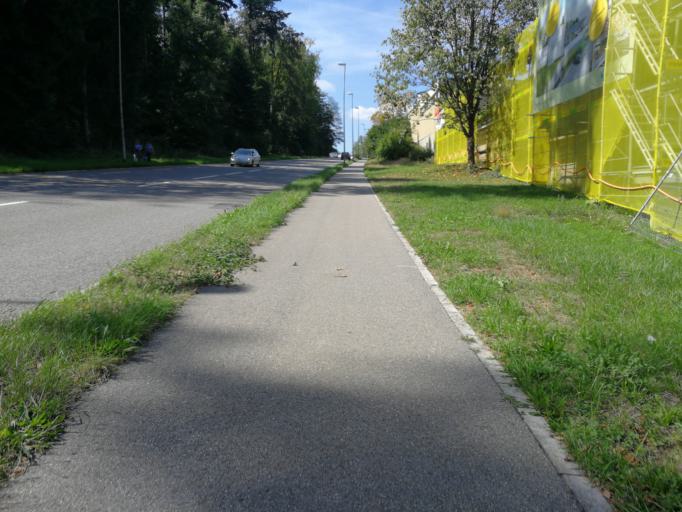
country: CH
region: Zurich
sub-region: Bezirk Horgen
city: Au
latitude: 47.2373
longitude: 8.6450
